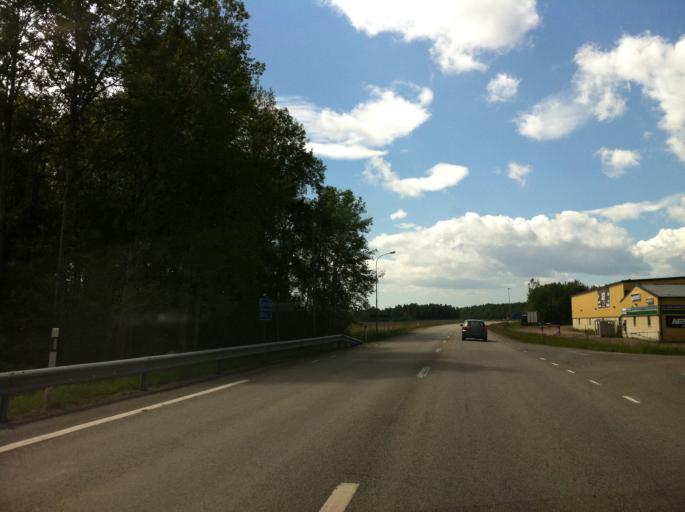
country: SE
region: Vaermland
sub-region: Saffle Kommun
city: Saeffle
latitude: 59.1813
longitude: 13.0117
